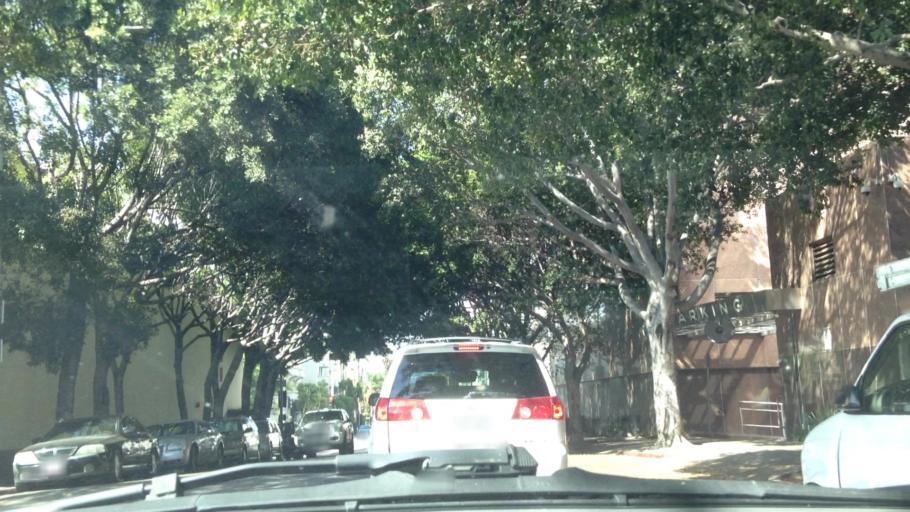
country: US
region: California
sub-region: Los Angeles County
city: Echo Park
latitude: 34.0602
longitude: -118.2828
